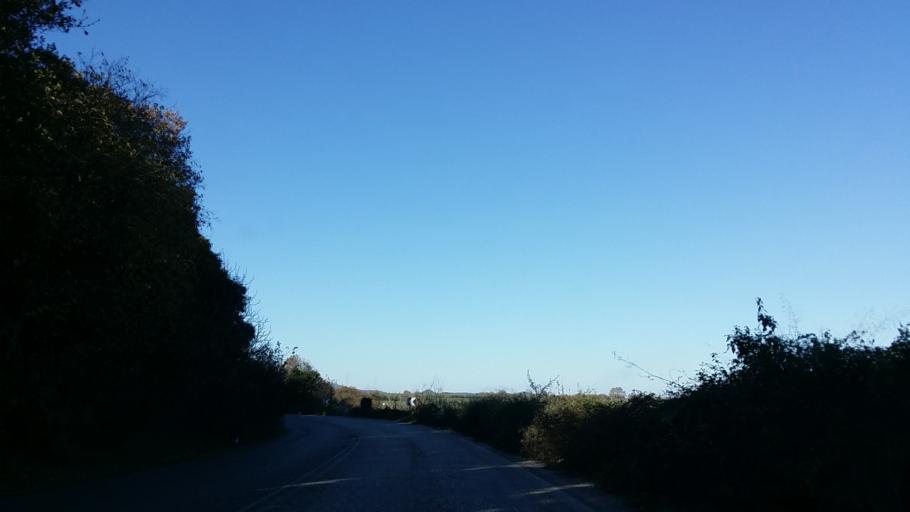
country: GR
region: West Greece
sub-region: Nomos Aitolias kai Akarnanias
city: Monastirakion
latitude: 38.8710
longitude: 21.0482
